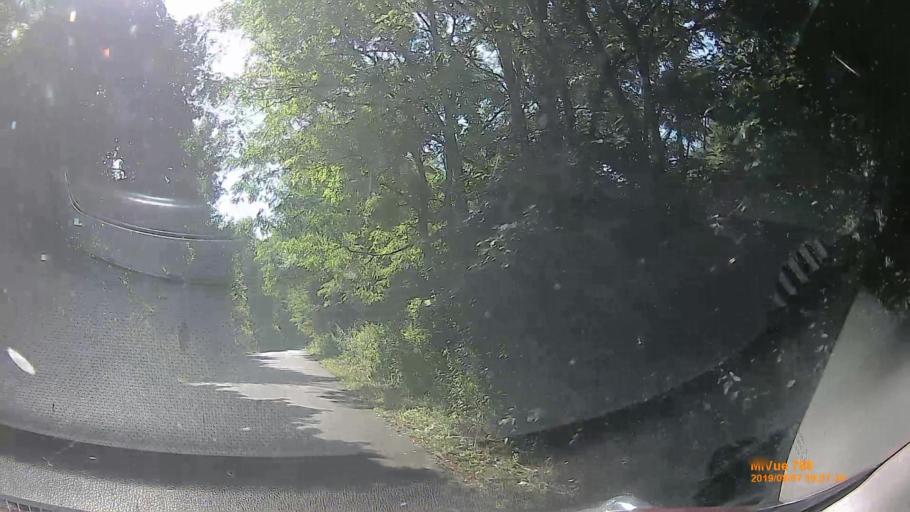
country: HU
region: Veszprem
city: Ajka
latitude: 47.0708
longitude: 17.5840
